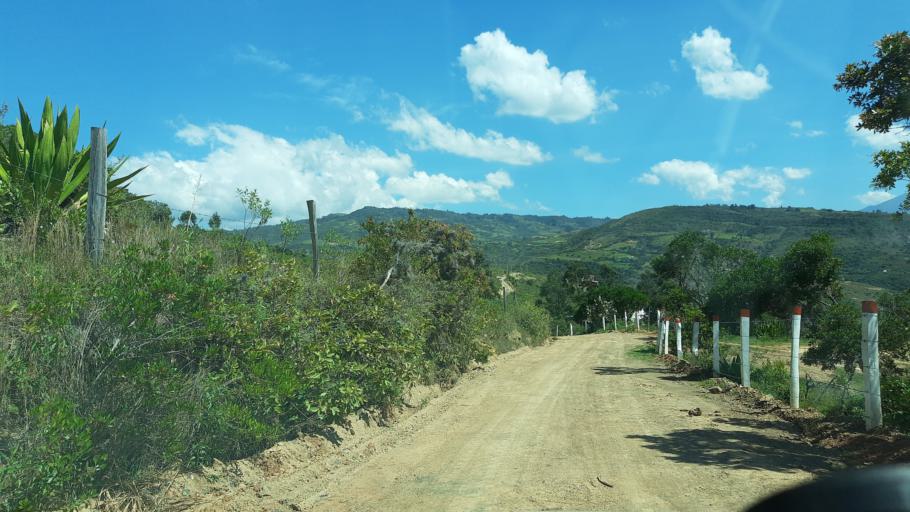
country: CO
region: Boyaca
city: Santa Sofia
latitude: 5.6947
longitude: -73.5780
